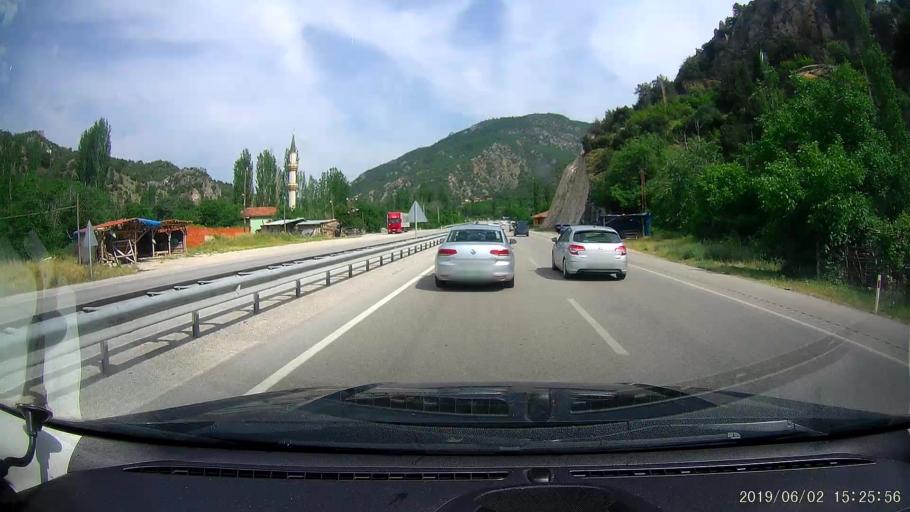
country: TR
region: Amasya
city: Saraycik
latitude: 40.9895
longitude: 35.0285
